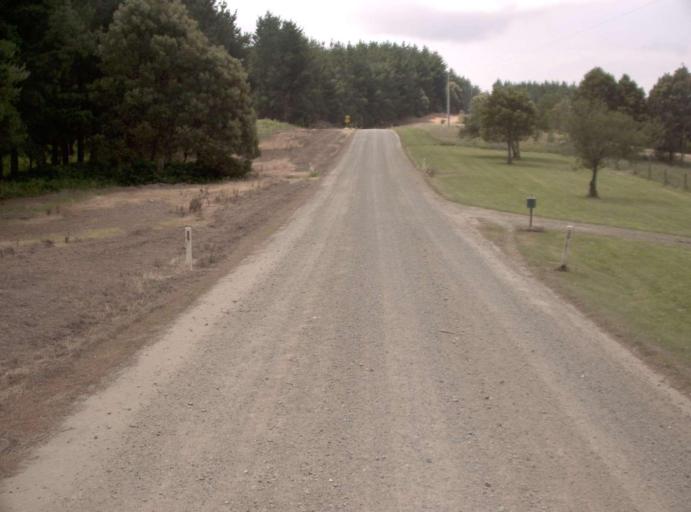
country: AU
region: Victoria
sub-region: Latrobe
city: Traralgon
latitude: -38.3917
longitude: 146.6600
